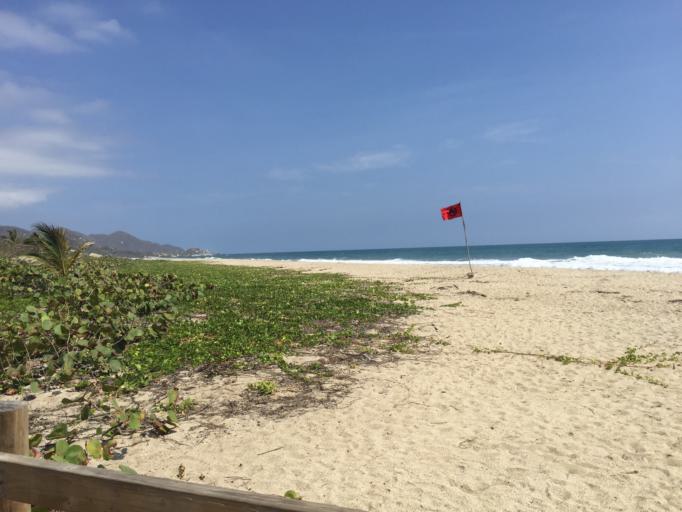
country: CO
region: Magdalena
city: Santa Marta
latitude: 11.3124
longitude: -73.9409
